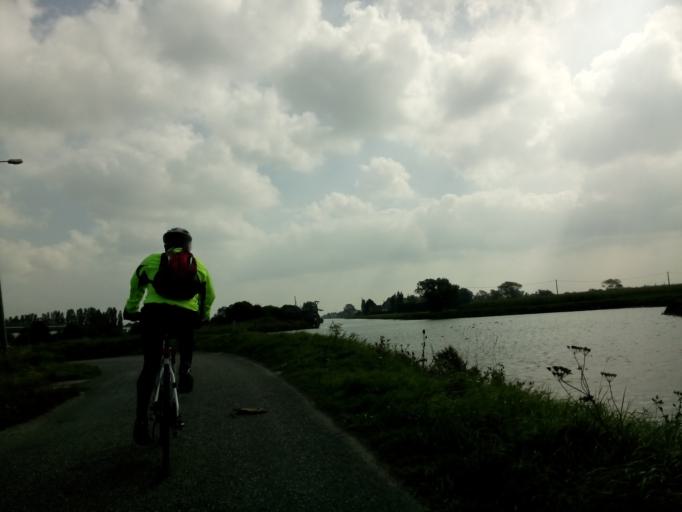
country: FR
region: Nord-Pas-de-Calais
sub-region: Departement du Pas-de-Calais
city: Les Attaques
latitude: 50.9129
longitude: 1.9160
